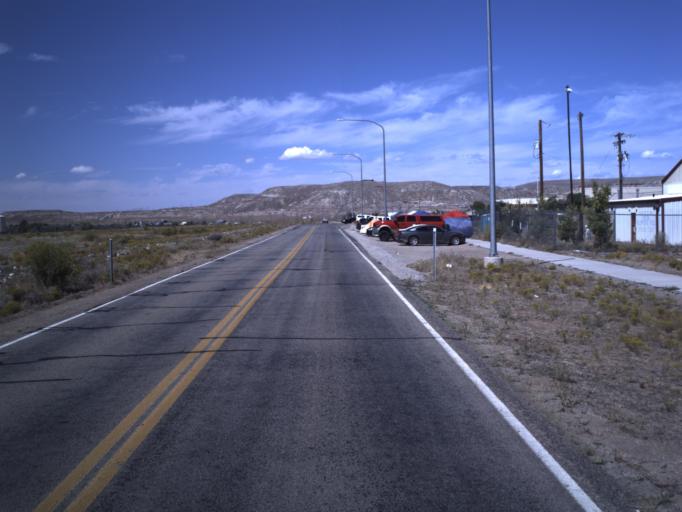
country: US
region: Utah
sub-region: San Juan County
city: Blanding
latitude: 37.2643
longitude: -109.3097
